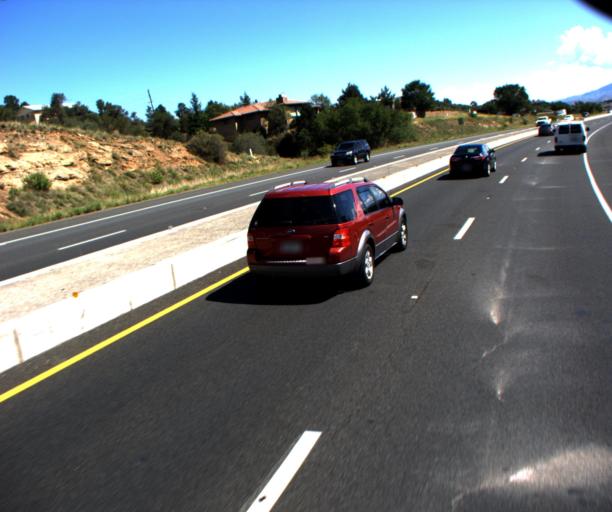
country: US
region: Arizona
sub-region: Yavapai County
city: Prescott Valley
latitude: 34.5599
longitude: -112.3793
